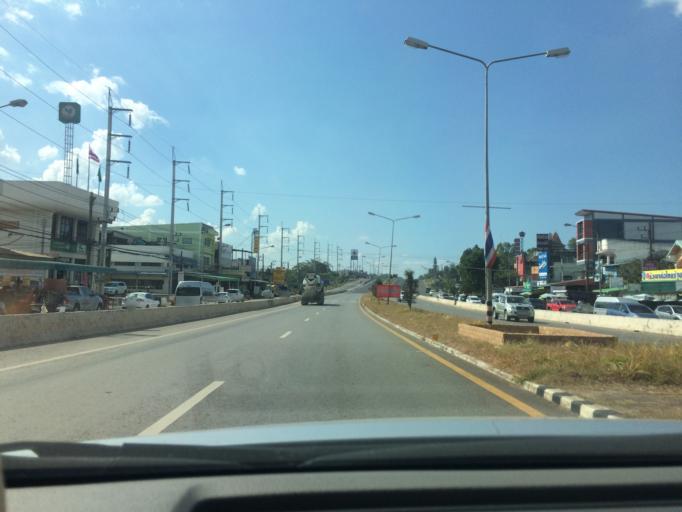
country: TH
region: Phetchabun
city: Khao Kho
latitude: 16.7694
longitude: 101.0455
